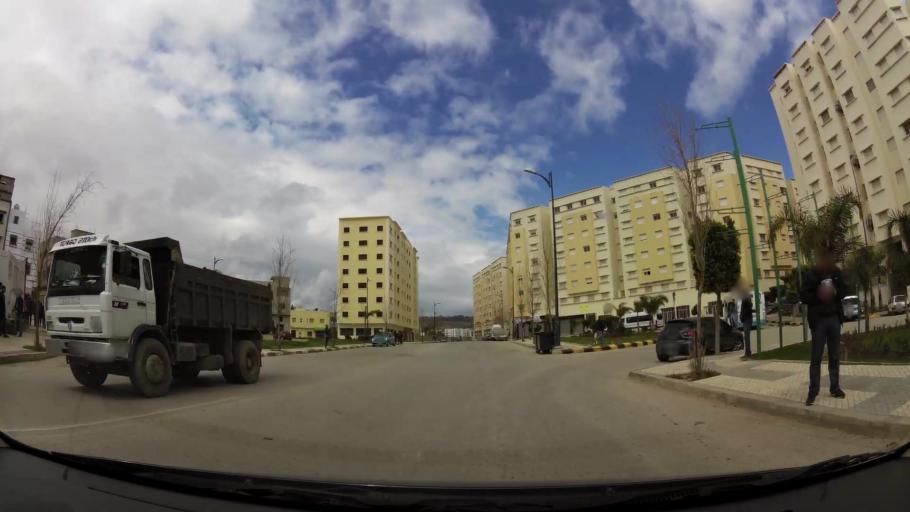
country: MA
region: Tanger-Tetouan
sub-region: Tanger-Assilah
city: Boukhalef
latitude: 35.7652
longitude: -5.8570
